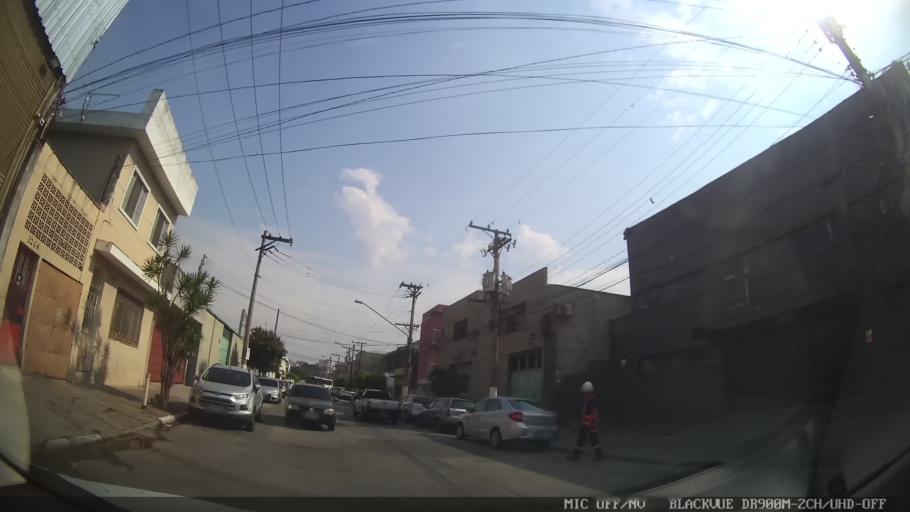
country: BR
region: Sao Paulo
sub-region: Sao Caetano Do Sul
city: Sao Caetano do Sul
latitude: -23.5935
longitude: -46.5922
